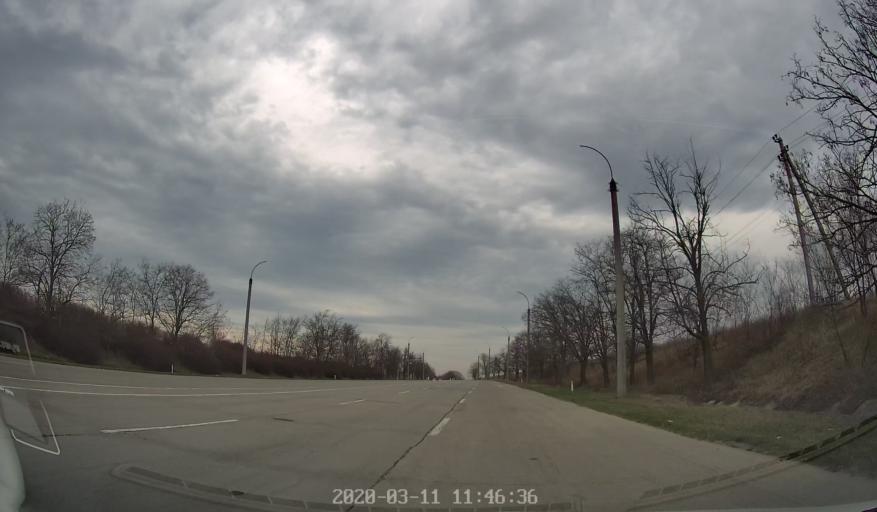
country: MD
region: Chisinau
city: Chisinau
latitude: 46.9468
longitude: 28.8672
